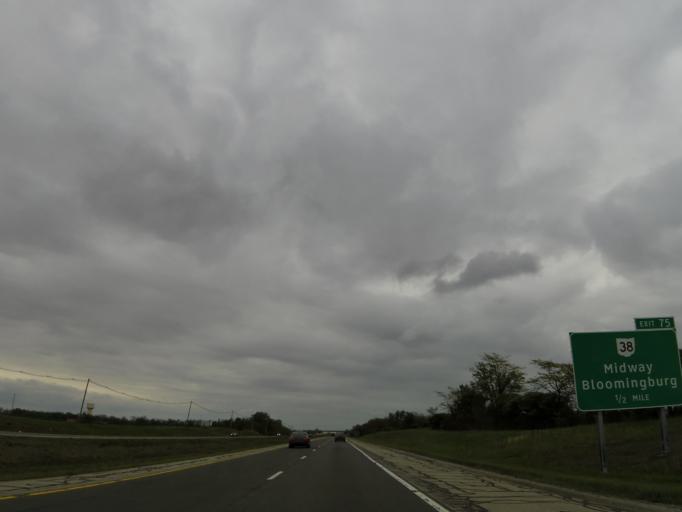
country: US
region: Ohio
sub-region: Madison County
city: Bethel
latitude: 39.6914
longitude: -83.4674
